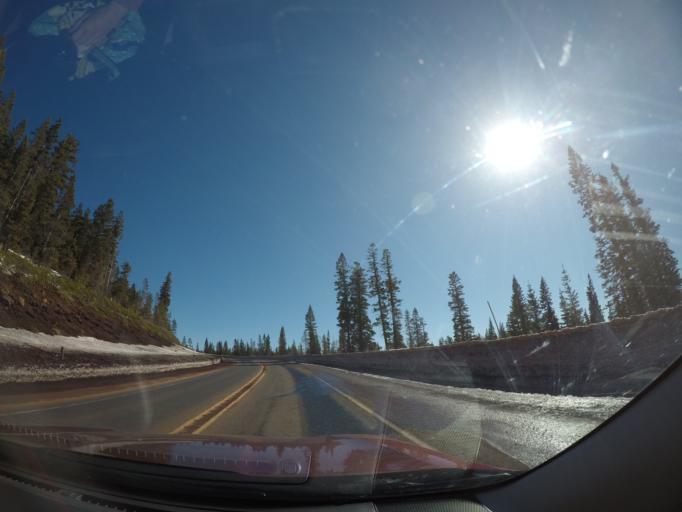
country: US
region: Oregon
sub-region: Deschutes County
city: Sunriver
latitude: 43.9803
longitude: -121.5877
